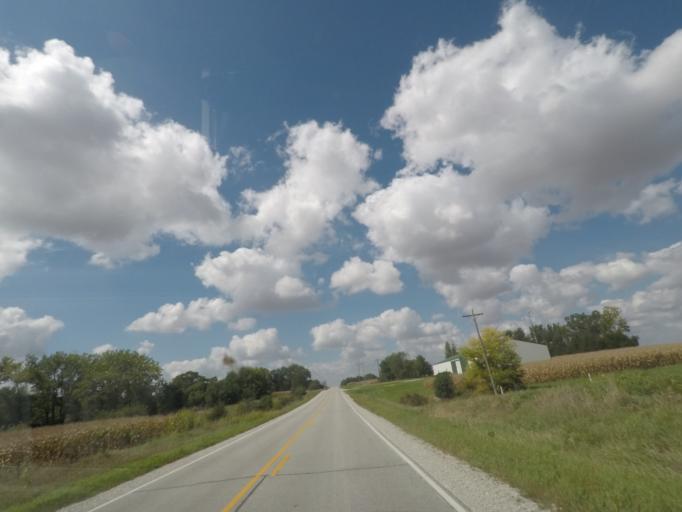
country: US
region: Iowa
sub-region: Story County
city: Nevada
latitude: 42.0226
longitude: -93.3424
